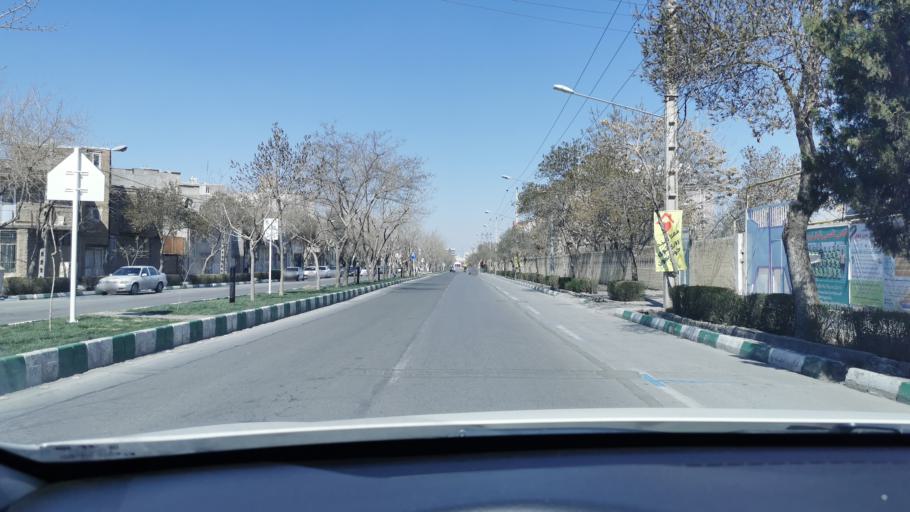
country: IR
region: Razavi Khorasan
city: Mashhad
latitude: 36.2782
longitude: 59.5769
